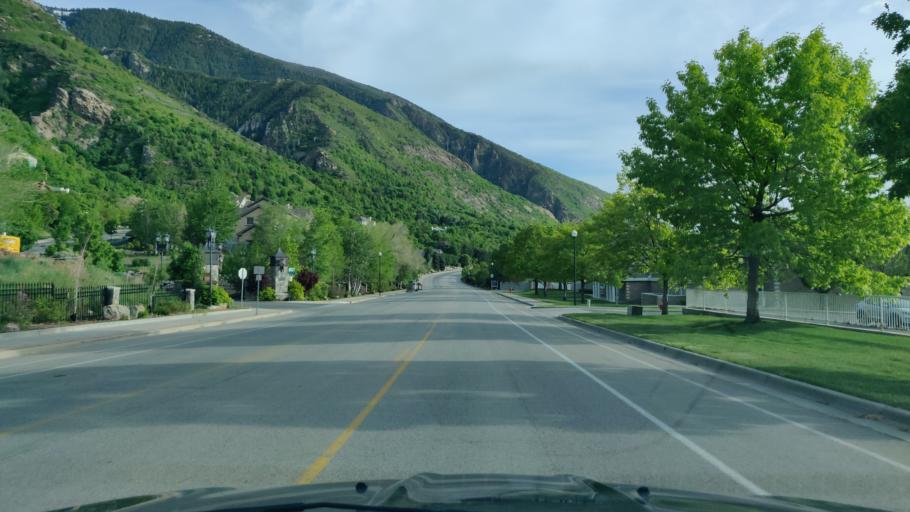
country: US
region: Utah
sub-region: Salt Lake County
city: Granite
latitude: 40.5488
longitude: -111.8062
